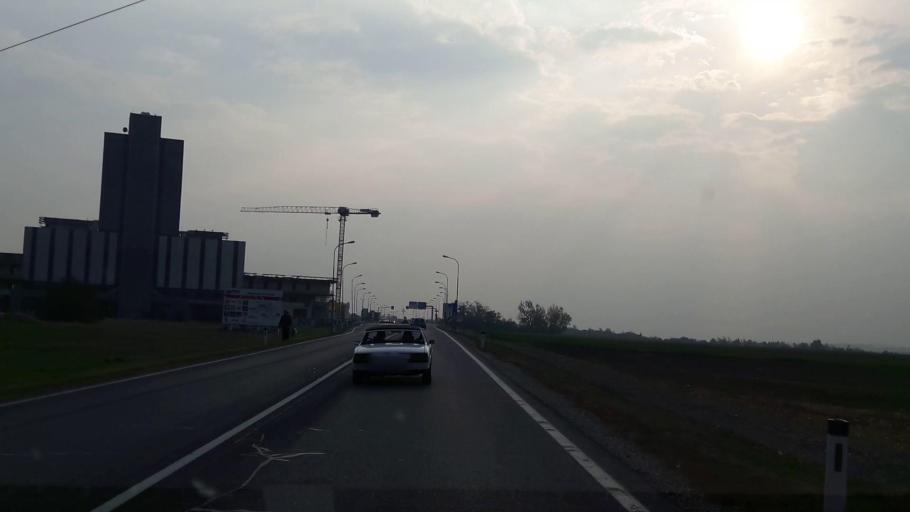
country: AT
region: Burgenland
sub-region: Politischer Bezirk Neusiedl am See
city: Parndorf
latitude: 47.9843
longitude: 16.8504
